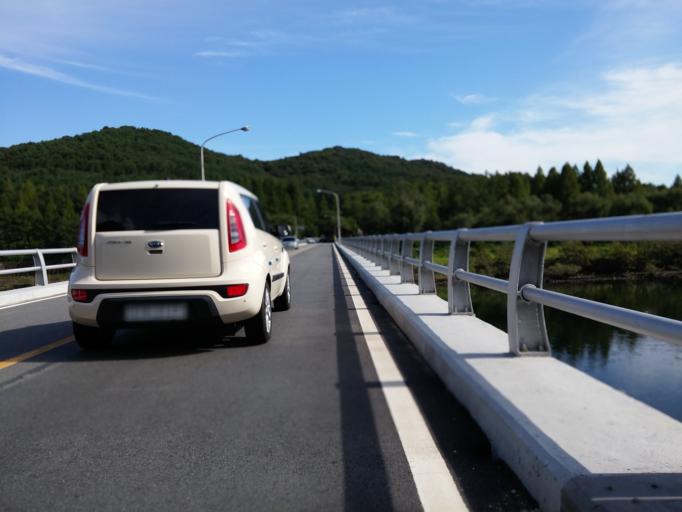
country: KR
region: Daejeon
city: Sintansin
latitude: 36.4763
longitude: 127.4749
